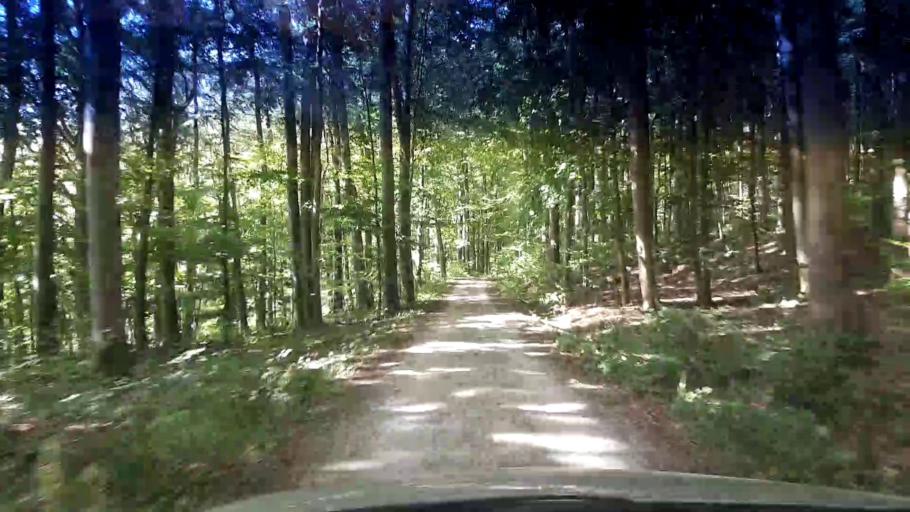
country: DE
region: Bavaria
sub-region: Upper Franconia
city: Schesslitz
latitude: 49.9475
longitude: 11.0668
